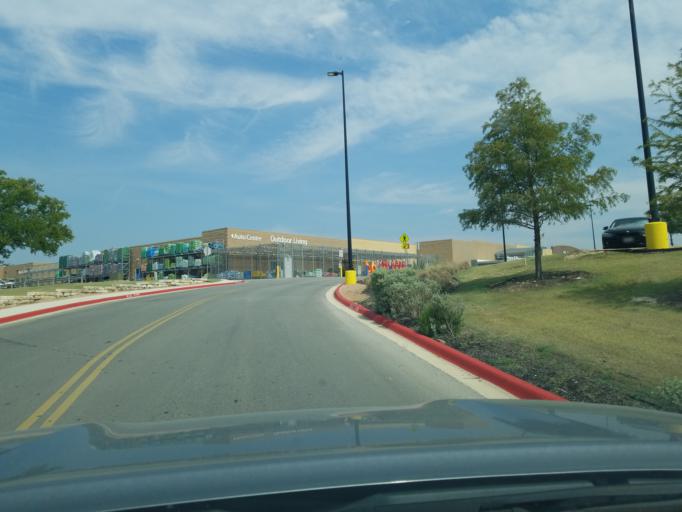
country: US
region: Texas
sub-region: Comal County
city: Bulverde
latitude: 29.8004
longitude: -98.4211
